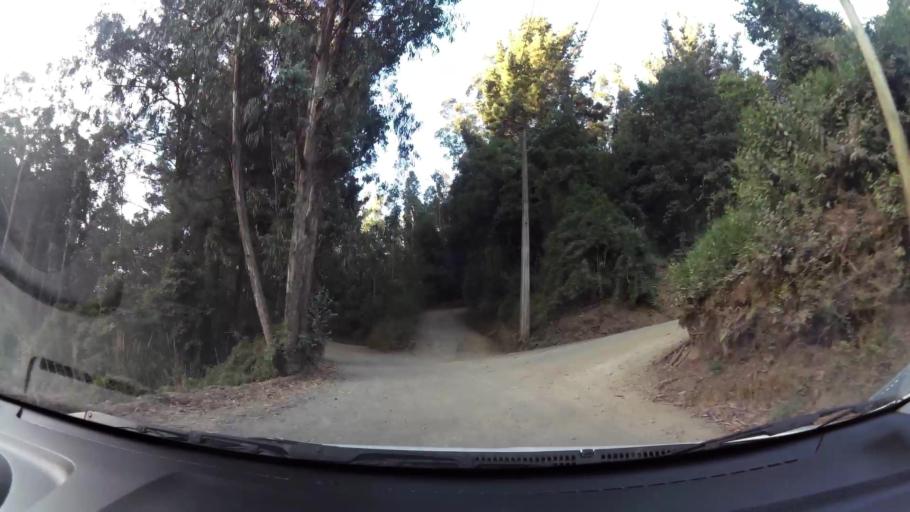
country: CL
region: Biobio
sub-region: Provincia de Concepcion
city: Concepcion
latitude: -36.8562
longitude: -73.0869
